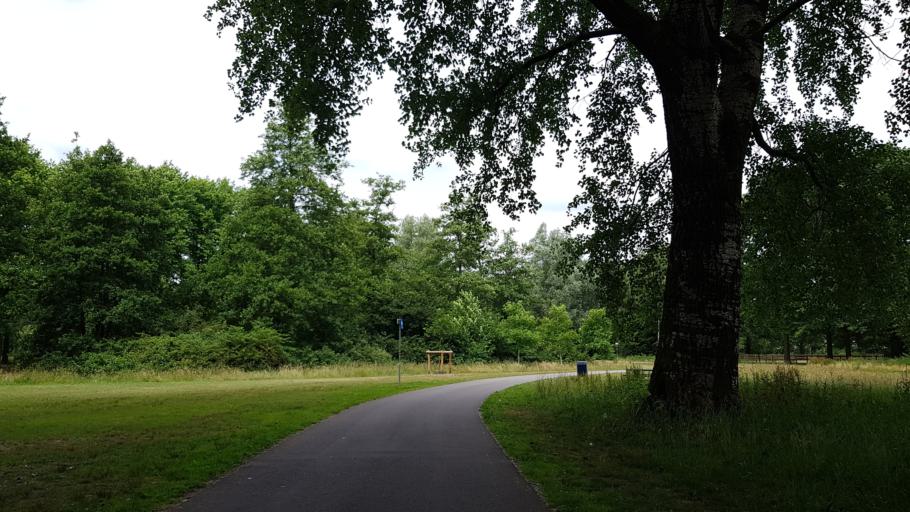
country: NL
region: Gelderland
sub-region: Gemeente Apeldoorn
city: Apeldoorn
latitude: 52.1972
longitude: 5.9980
